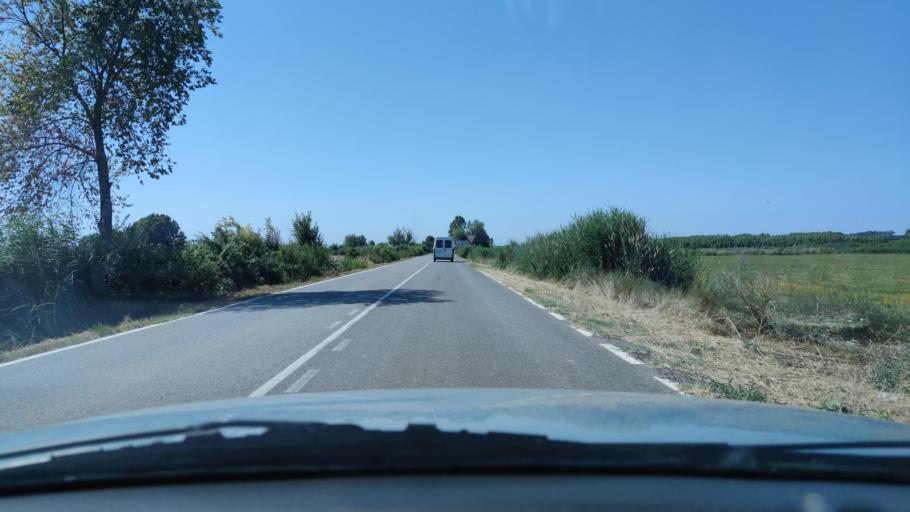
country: ES
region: Catalonia
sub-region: Provincia de Lleida
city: Penelles
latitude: 41.7319
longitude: 0.9830
